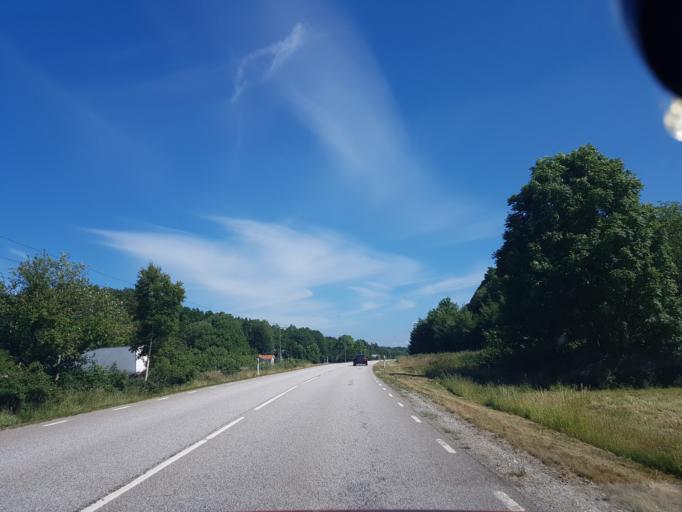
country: SE
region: Vaestra Goetaland
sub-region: Lysekils Kommun
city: Lysekil
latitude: 58.1597
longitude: 11.4737
